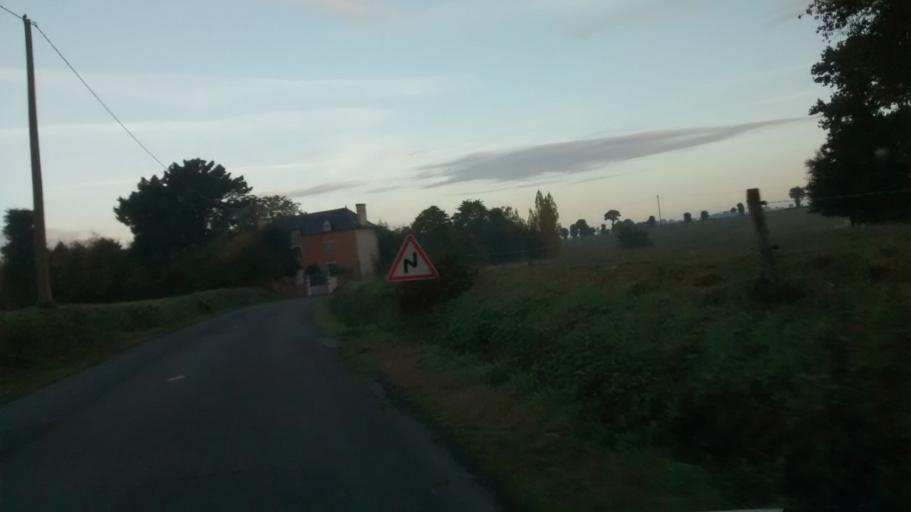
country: FR
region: Brittany
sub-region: Departement d'Ille-et-Vilaine
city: Betton
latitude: 48.1870
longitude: -1.6578
